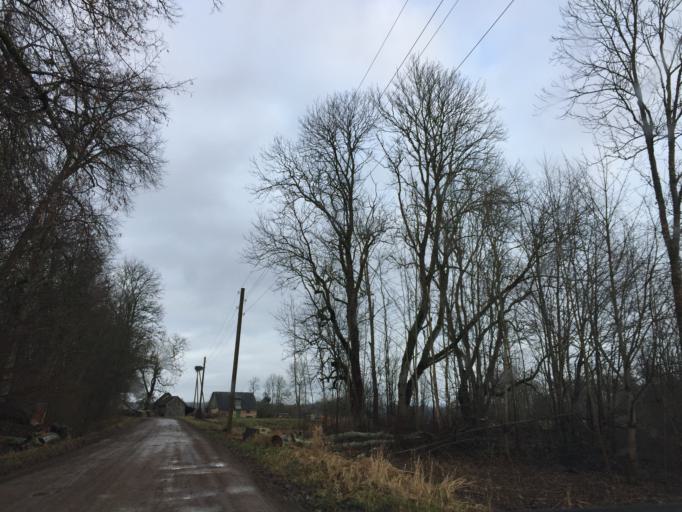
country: LV
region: Vainode
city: Vainode
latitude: 56.6140
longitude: 21.7950
